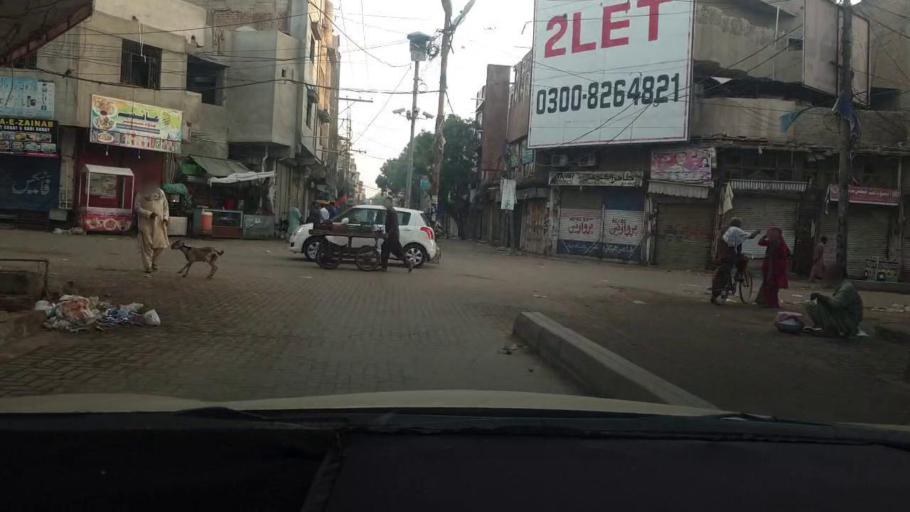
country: PK
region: Sindh
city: Larkana
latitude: 27.5527
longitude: 68.2152
